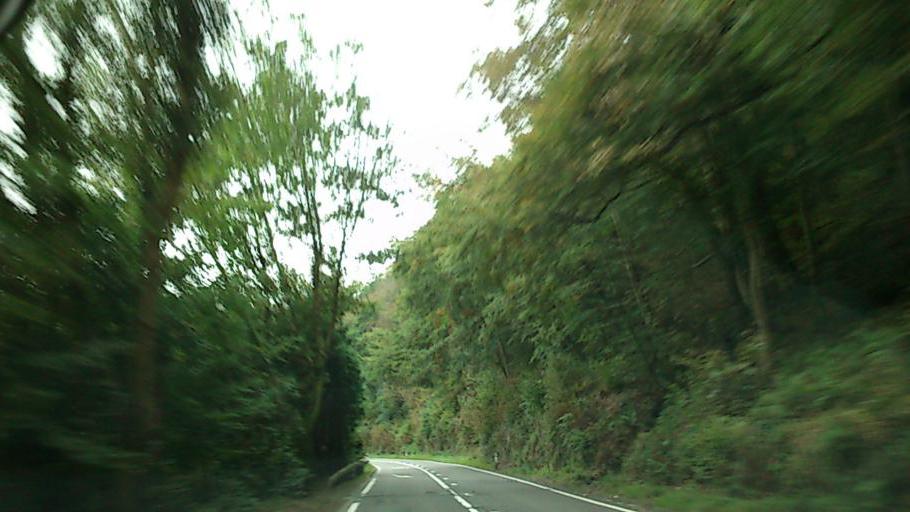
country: GB
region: Wales
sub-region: Sir Powys
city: Machynlleth
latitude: 52.5760
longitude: -3.8927
